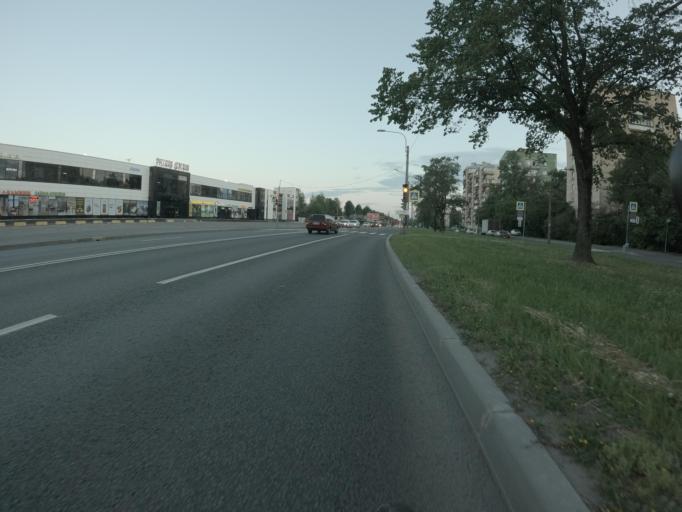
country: RU
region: St.-Petersburg
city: Dachnoye
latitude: 59.8453
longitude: 30.2797
